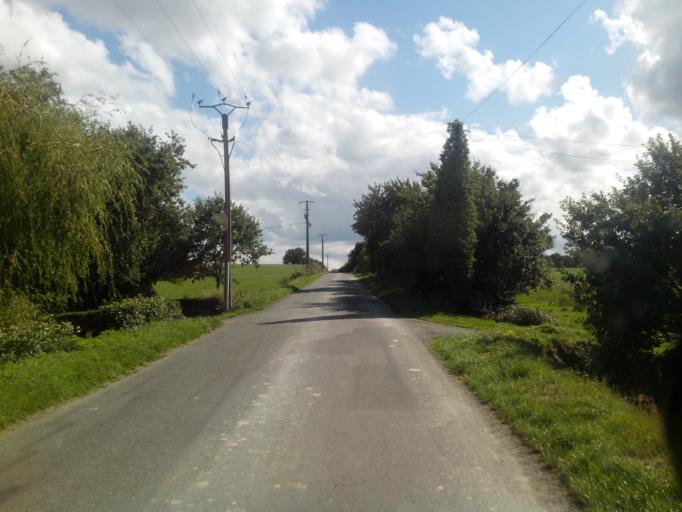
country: FR
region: Brittany
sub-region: Departement d'Ille-et-Vilaine
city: Gael
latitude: 48.1171
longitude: -2.1404
